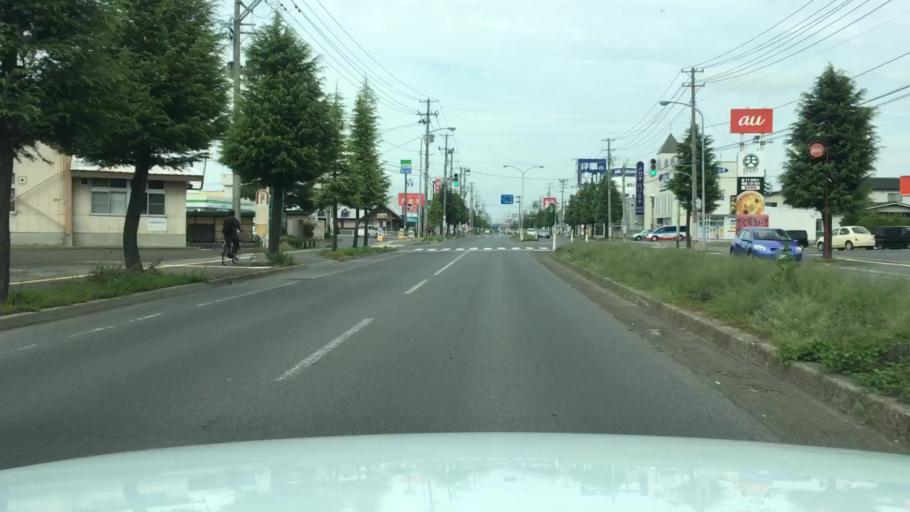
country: JP
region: Aomori
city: Hirosaki
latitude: 40.6129
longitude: 140.4829
